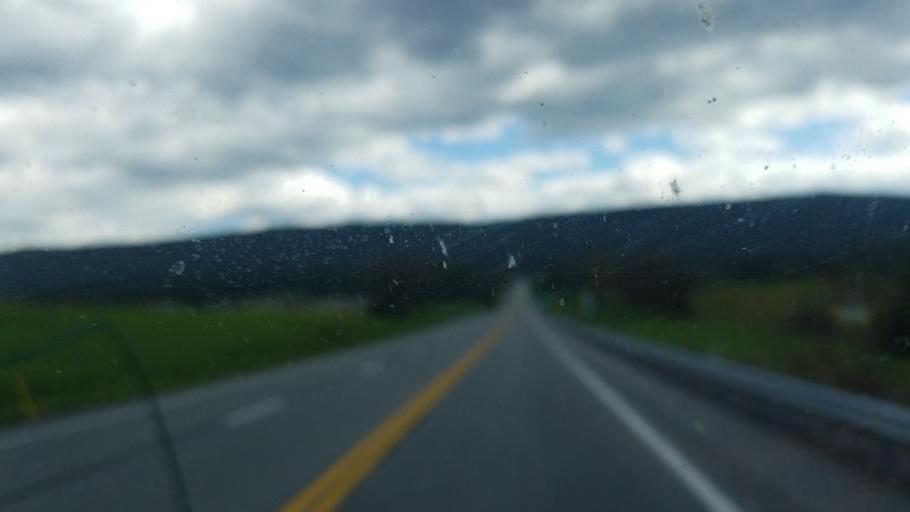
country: US
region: Pennsylvania
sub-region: Fulton County
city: McConnellsburg
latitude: 39.9443
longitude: -78.0054
